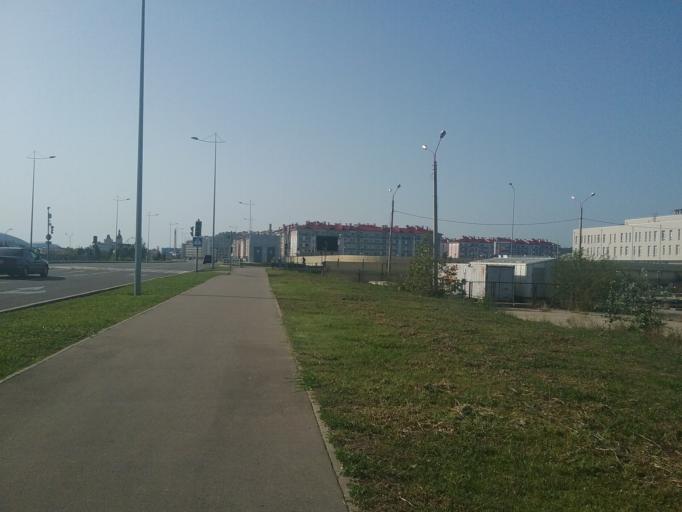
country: RU
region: Krasnodarskiy
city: Vysokoye
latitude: 43.3980
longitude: 39.9842
